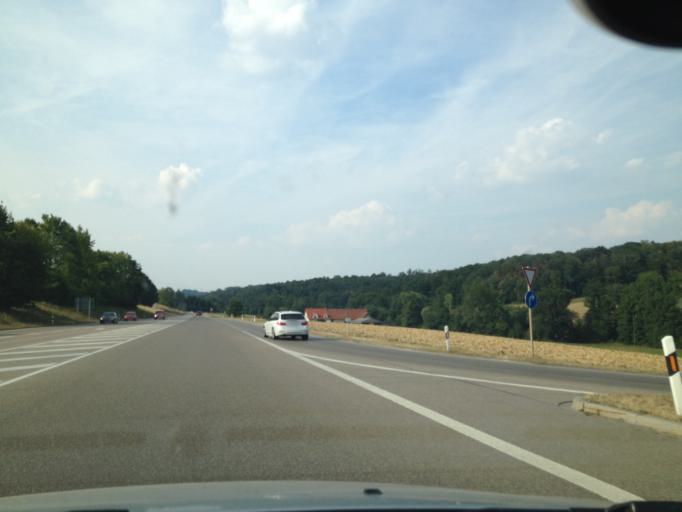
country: DE
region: Bavaria
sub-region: Swabia
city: Donauwoerth
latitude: 48.7384
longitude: 10.7777
